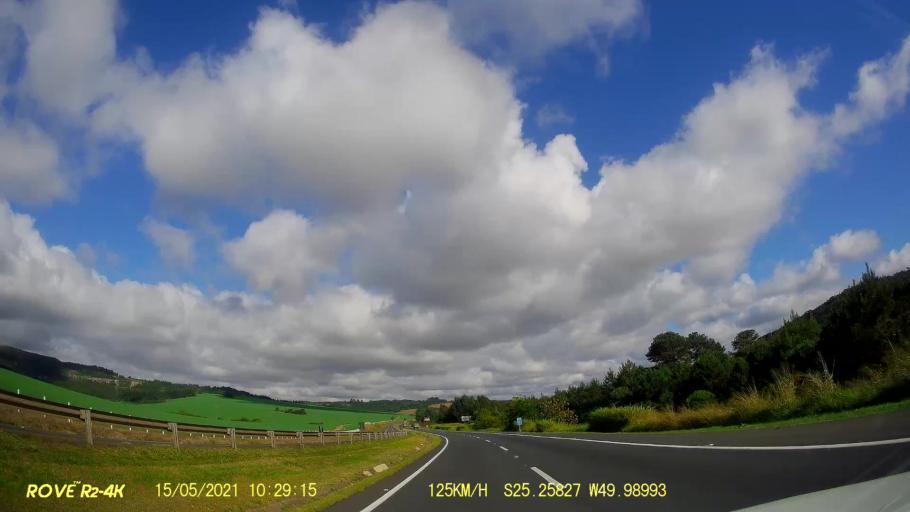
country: BR
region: Parana
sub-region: Palmeira
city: Palmeira
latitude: -25.2584
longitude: -49.9899
